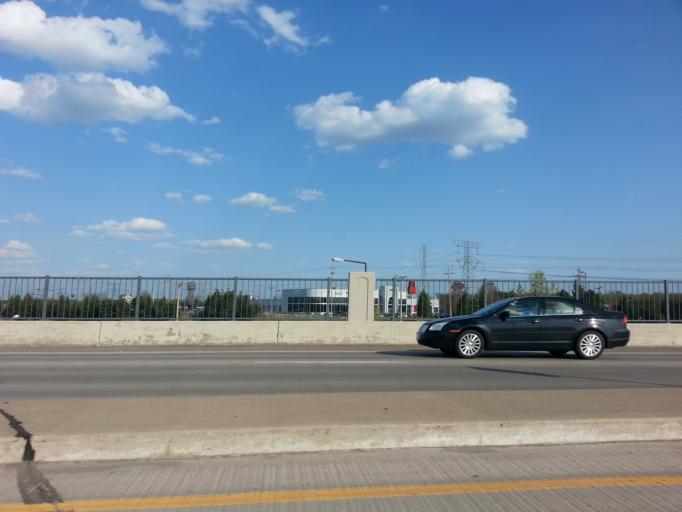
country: US
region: Minnesota
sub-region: Washington County
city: Stillwater
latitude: 45.0362
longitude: -92.8465
